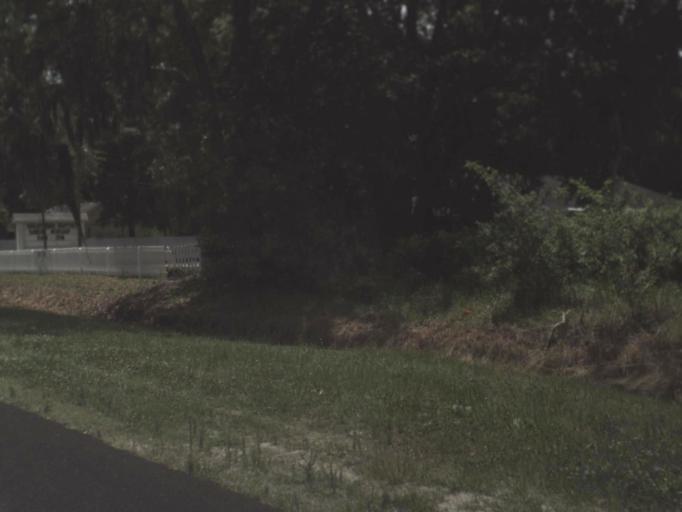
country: US
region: Florida
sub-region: Nassau County
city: Nassau Village-Ratliff
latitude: 30.4232
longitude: -81.7543
